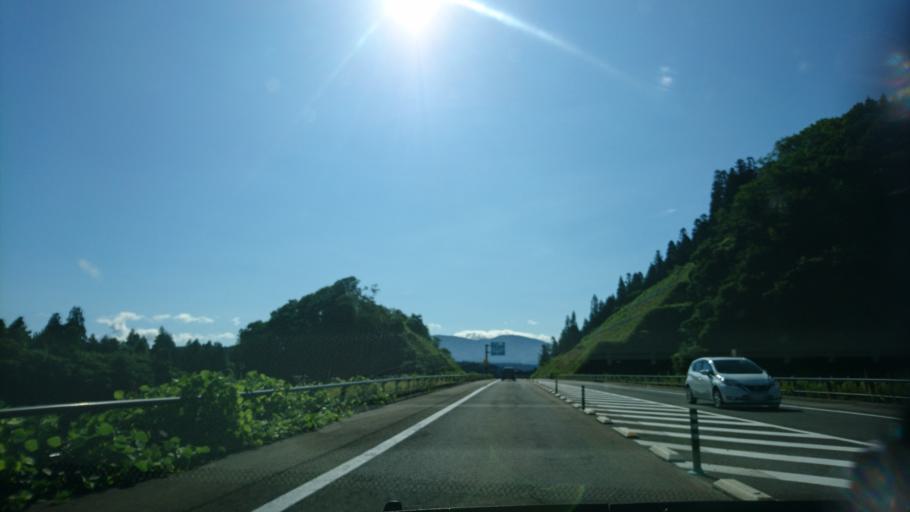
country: JP
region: Akita
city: Kakunodatemachi
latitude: 39.5956
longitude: 140.5315
